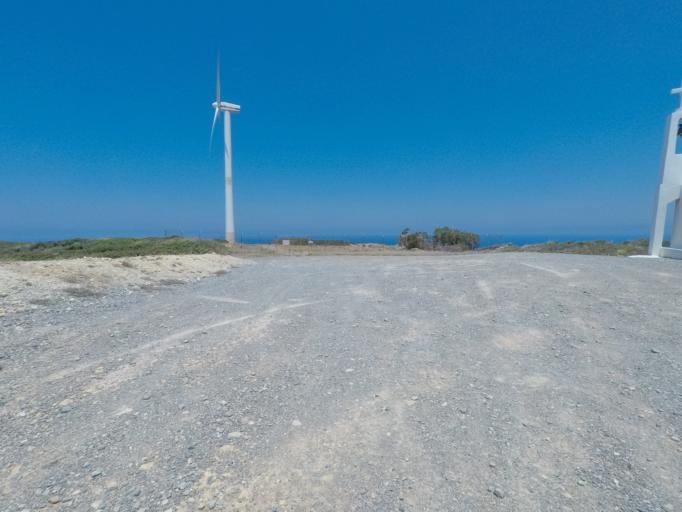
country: GR
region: Crete
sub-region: Nomos Lasithiou
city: Elounda
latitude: 35.3324
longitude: 25.7612
